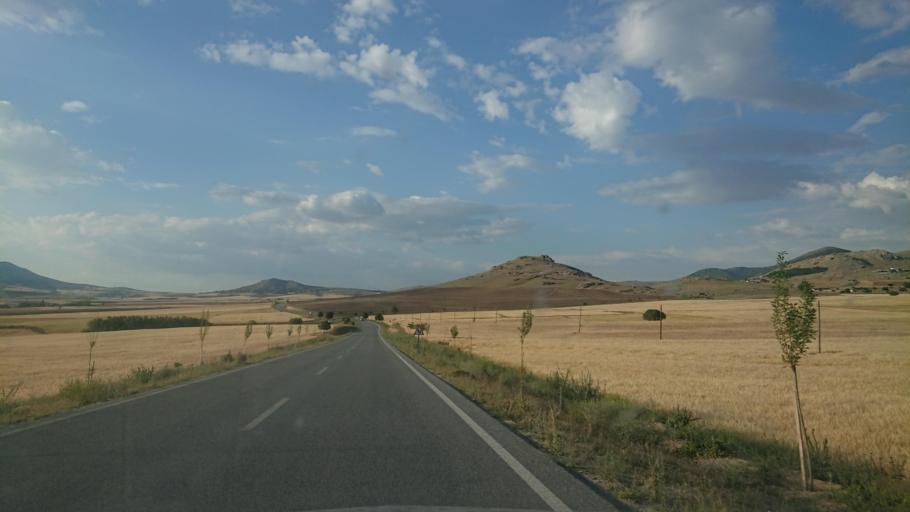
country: TR
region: Aksaray
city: Balci
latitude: 38.5439
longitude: 34.1021
